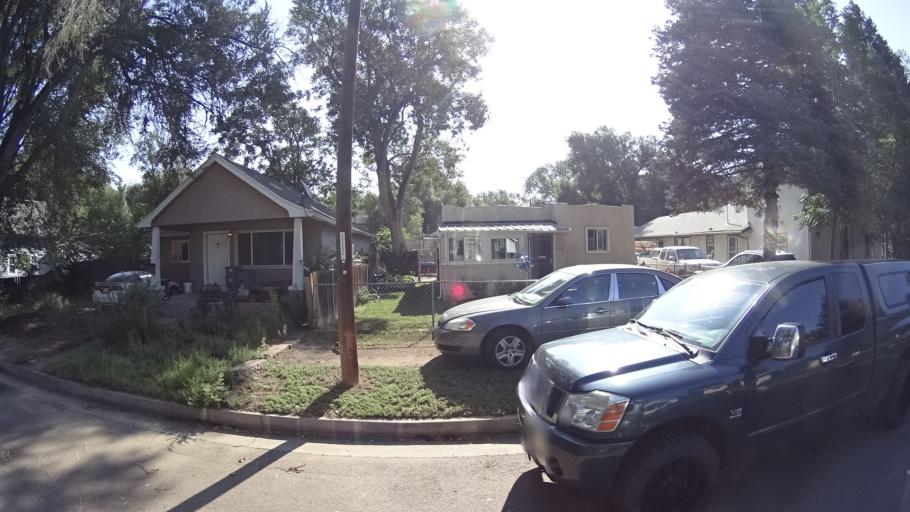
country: US
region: Colorado
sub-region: El Paso County
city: Colorado Springs
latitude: 38.8692
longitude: -104.8296
